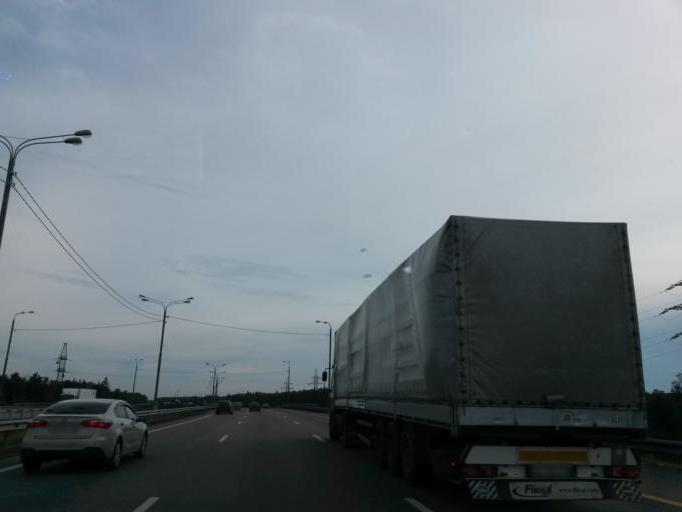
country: RU
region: Moskovskaya
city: Vostryakovo
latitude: 55.4148
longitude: 37.7944
